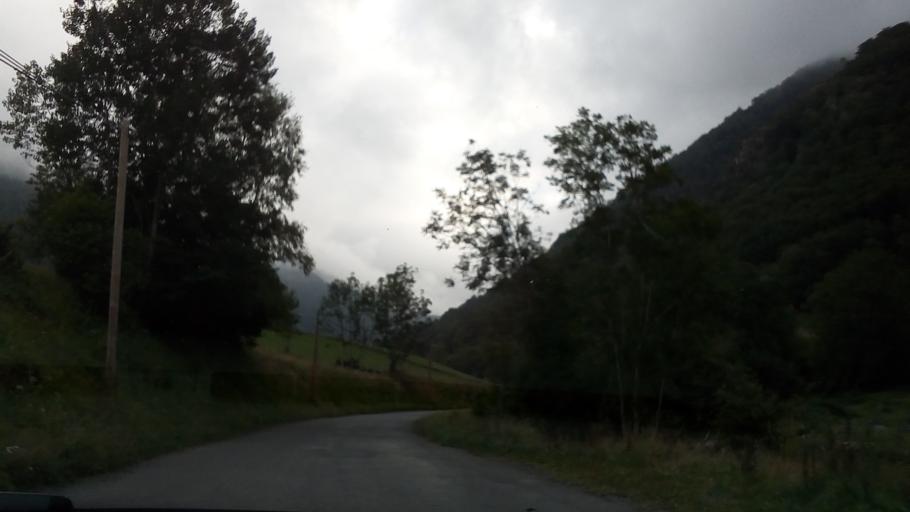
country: FR
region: Midi-Pyrenees
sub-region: Departement des Hautes-Pyrenees
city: Cauterets
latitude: 42.9270
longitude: -0.1825
